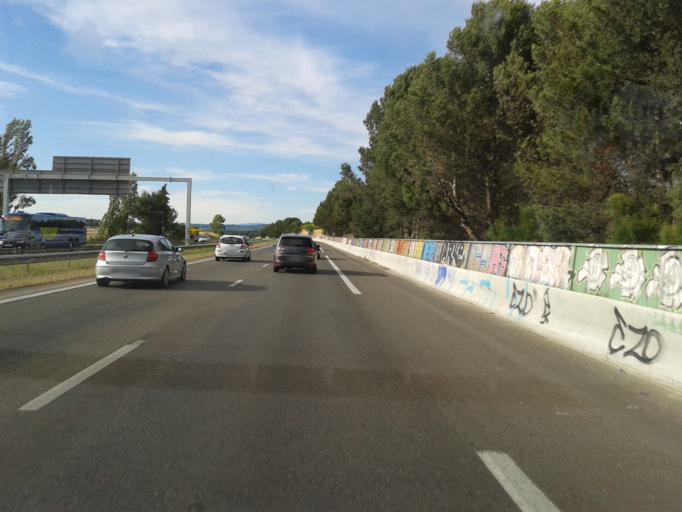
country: FR
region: Provence-Alpes-Cote d'Azur
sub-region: Departement des Bouches-du-Rhone
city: Bouc-Bel-Air
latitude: 43.4751
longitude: 5.4077
